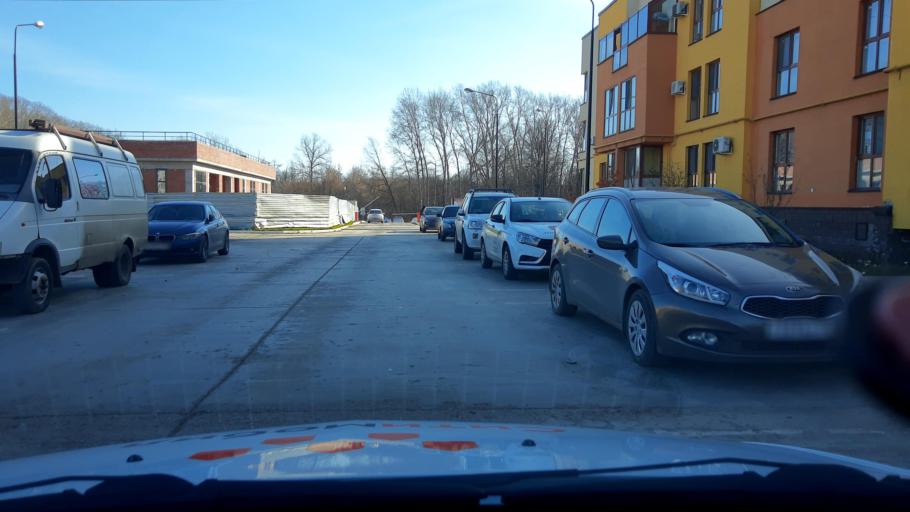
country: RU
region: Bashkortostan
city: Ufa
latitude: 54.7960
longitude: 55.9580
